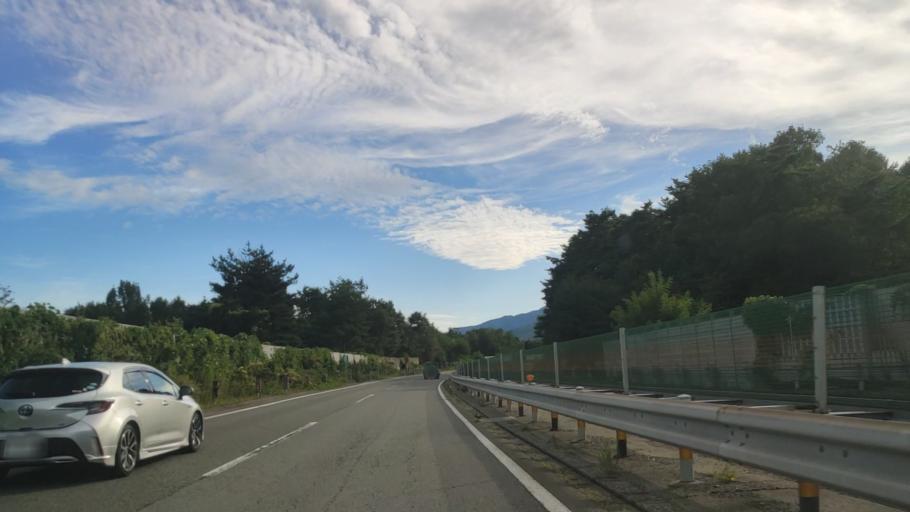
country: JP
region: Nagano
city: Ina
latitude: 35.7579
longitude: 137.9169
